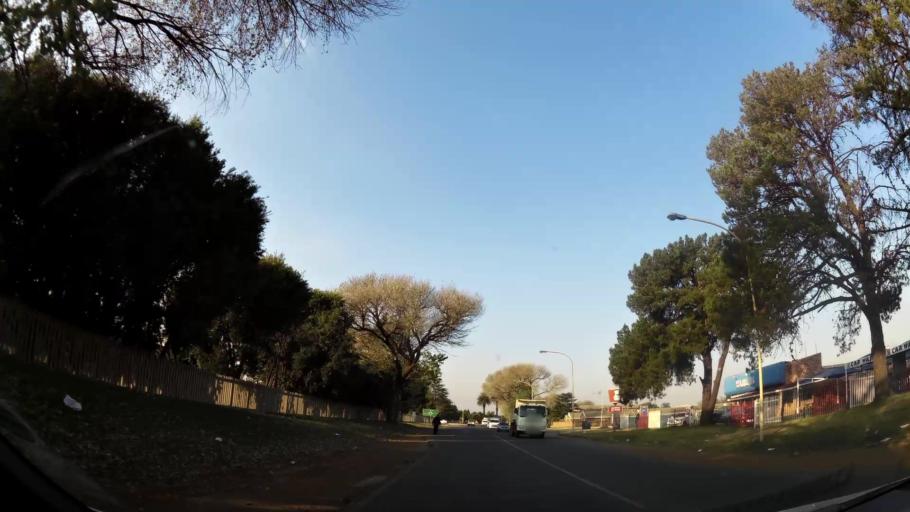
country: ZA
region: Gauteng
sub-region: Ekurhuleni Metropolitan Municipality
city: Springs
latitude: -26.2535
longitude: 28.4019
